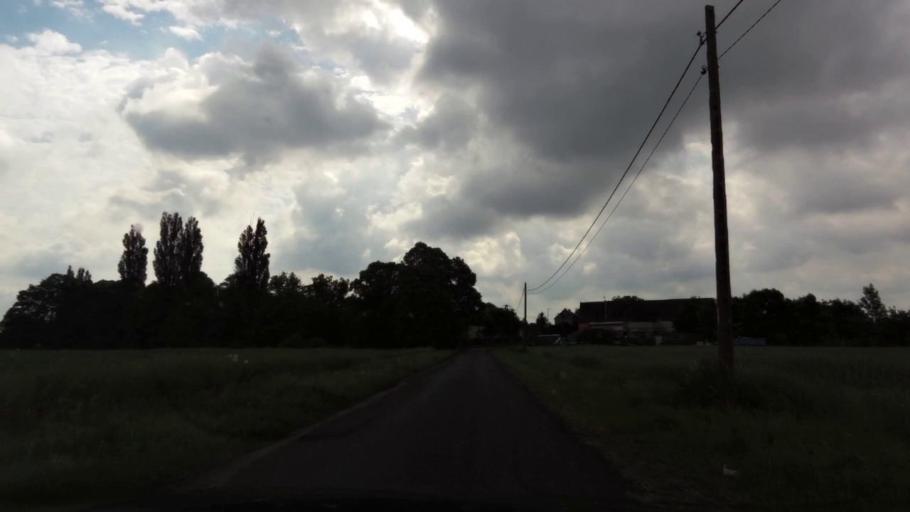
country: PL
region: West Pomeranian Voivodeship
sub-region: Powiat pyrzycki
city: Lipiany
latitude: 52.9567
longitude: 14.9527
